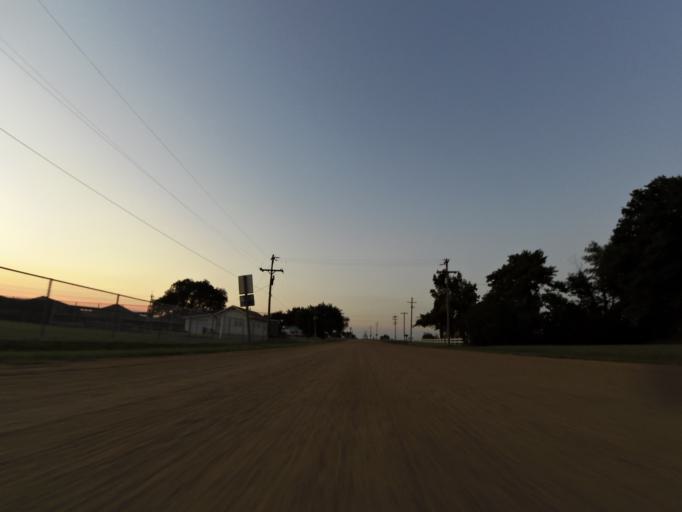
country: US
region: Kansas
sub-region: Reno County
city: South Hutchinson
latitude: 37.9953
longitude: -98.0319
